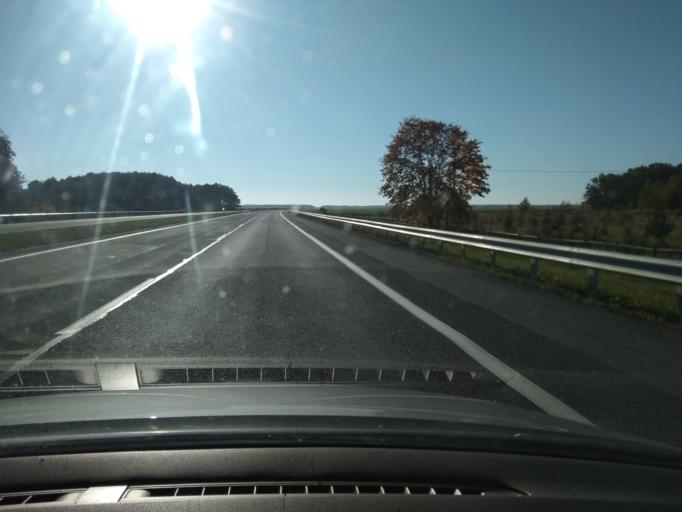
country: BY
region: Brest
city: Ivatsevichy
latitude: 52.6768
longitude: 25.3211
